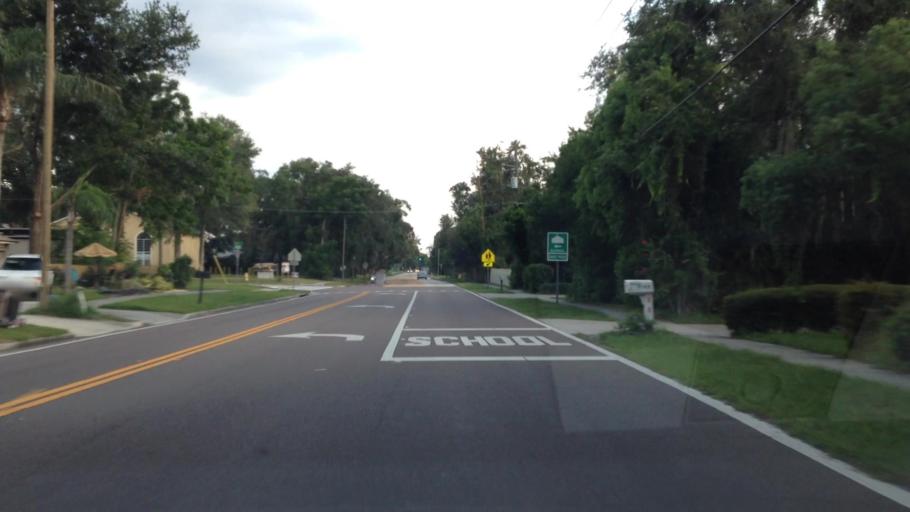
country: US
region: Florida
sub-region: Seminole County
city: Forest City
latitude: 28.6572
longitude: -81.4439
